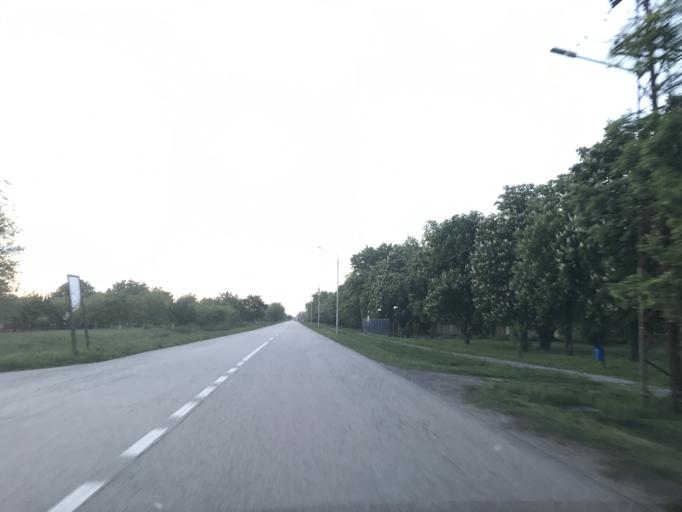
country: RS
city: Srpska Crnja
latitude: 45.7357
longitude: 20.6987
